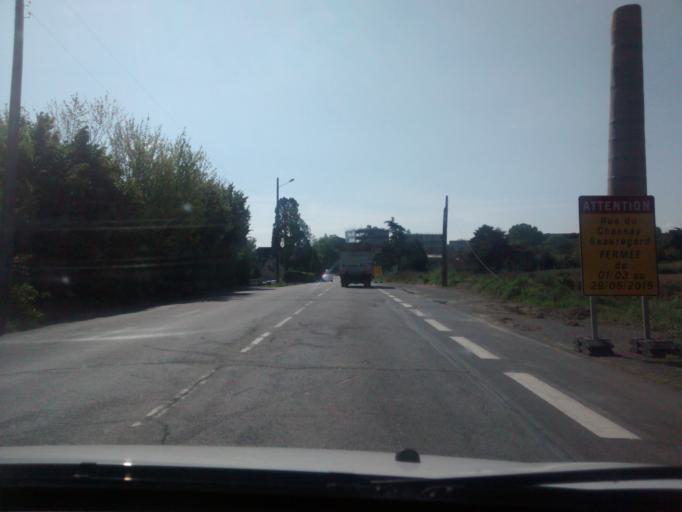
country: FR
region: Brittany
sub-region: Departement d'Ille-et-Vilaine
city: Saint-Gregoire
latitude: 48.1363
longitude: -1.6968
